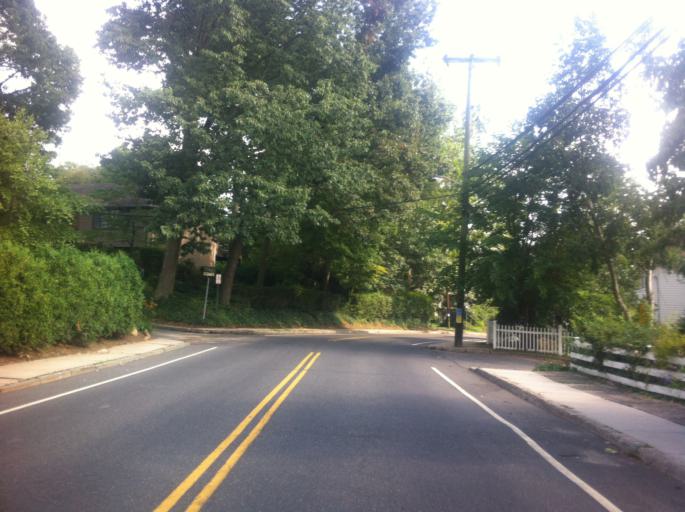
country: US
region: New York
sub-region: Nassau County
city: Sea Cliff
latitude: 40.8505
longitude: -73.6487
